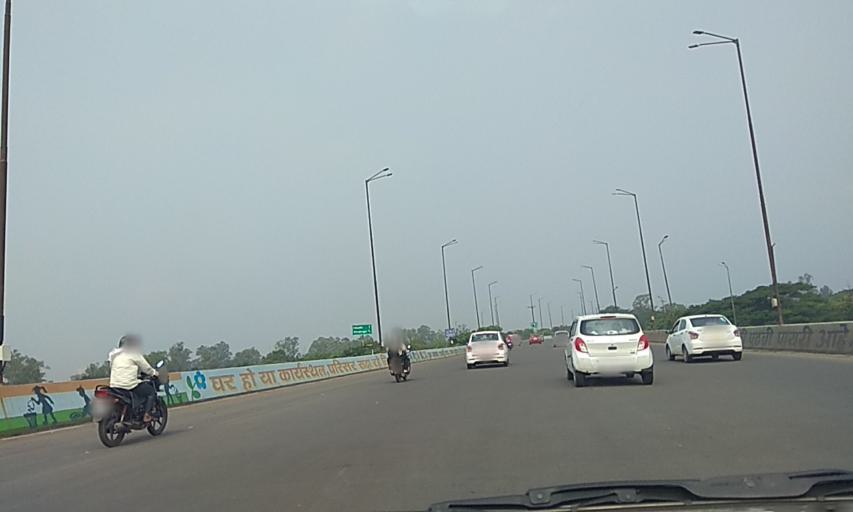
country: IN
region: Maharashtra
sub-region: Pune Division
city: Khadki
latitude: 18.5538
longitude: 73.8634
